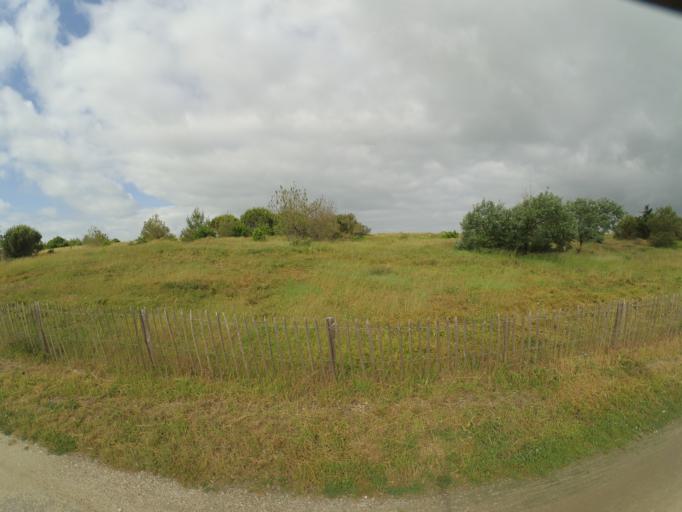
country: FR
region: Poitou-Charentes
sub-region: Departement de la Charente-Maritime
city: Aytre
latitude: 46.1204
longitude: -1.1238
